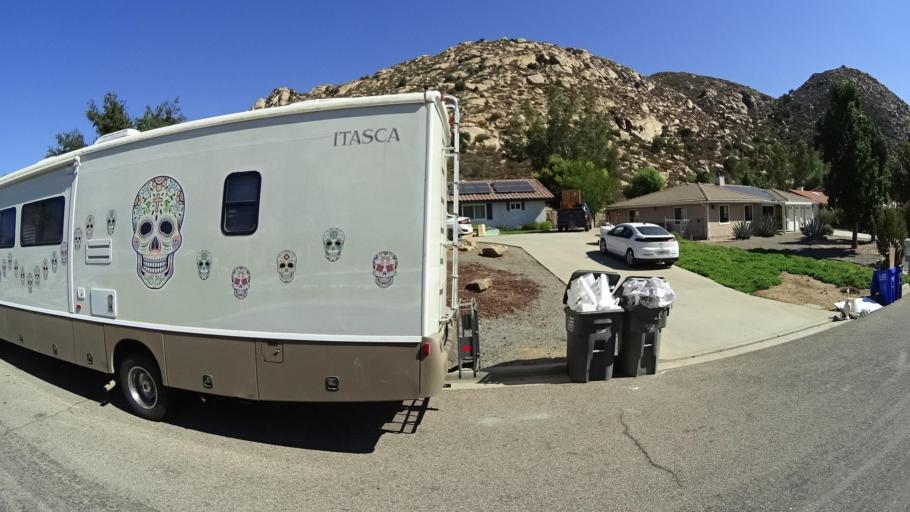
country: US
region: California
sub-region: San Diego County
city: San Diego Country Estates
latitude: 33.0083
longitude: -116.7837
